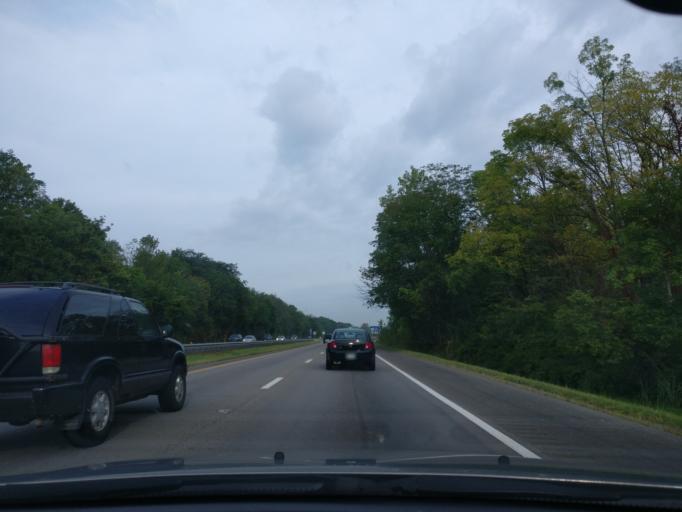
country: US
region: Ohio
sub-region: Greene County
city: Beavercreek
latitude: 39.7138
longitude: -84.0435
